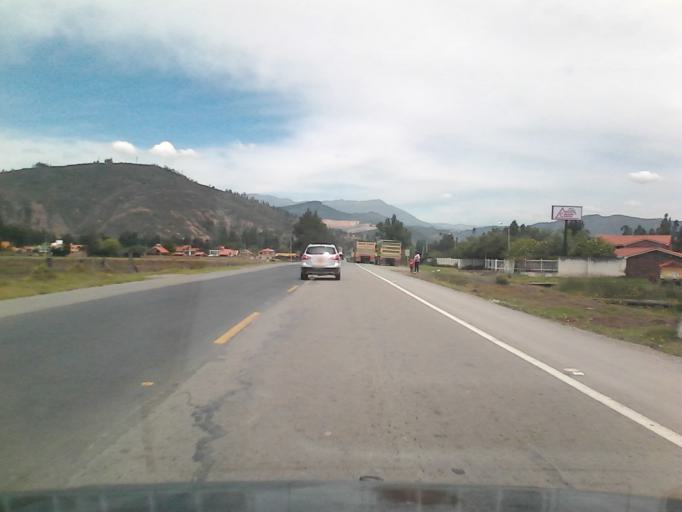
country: CO
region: Boyaca
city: Tibasosa
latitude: 5.7711
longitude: -72.9963
